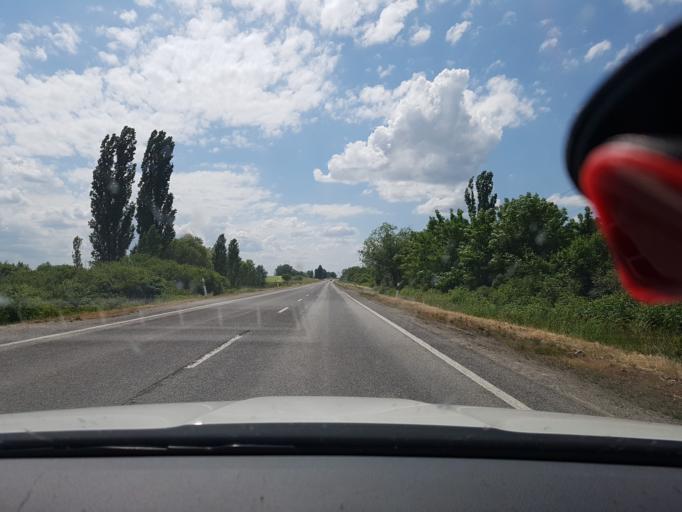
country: HU
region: Heves
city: Domoszlo
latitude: 47.7473
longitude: 20.1504
